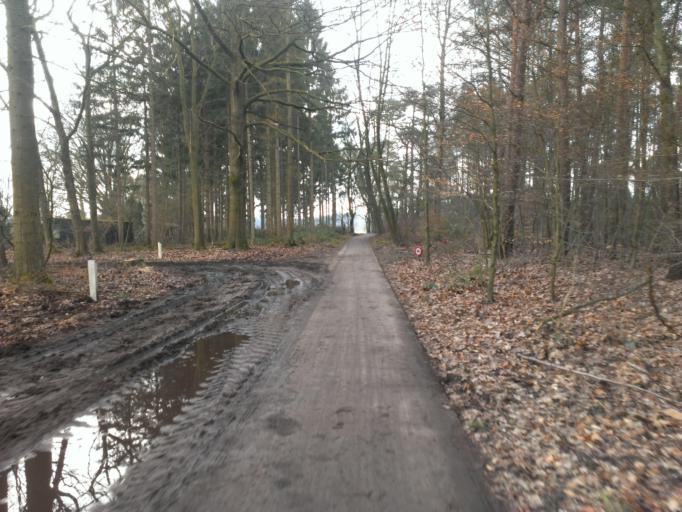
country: NL
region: Gelderland
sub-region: Gemeente Epe
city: Epe
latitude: 52.3876
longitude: 5.9970
